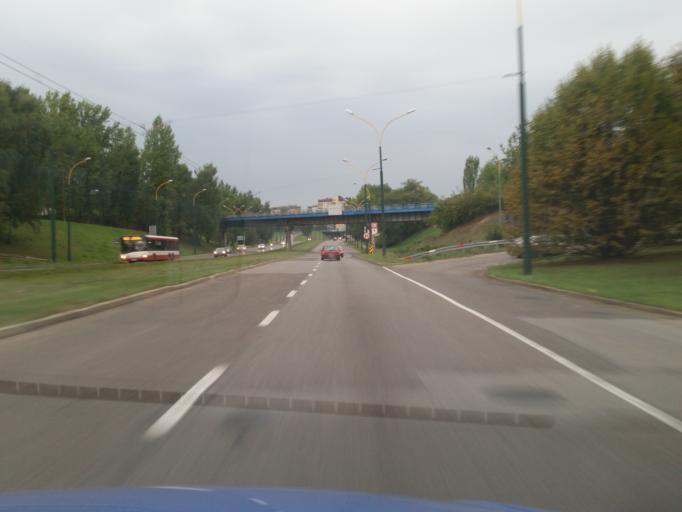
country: PL
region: Silesian Voivodeship
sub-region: Powiat bedzinski
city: Bedzin
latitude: 50.2898
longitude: 19.1562
